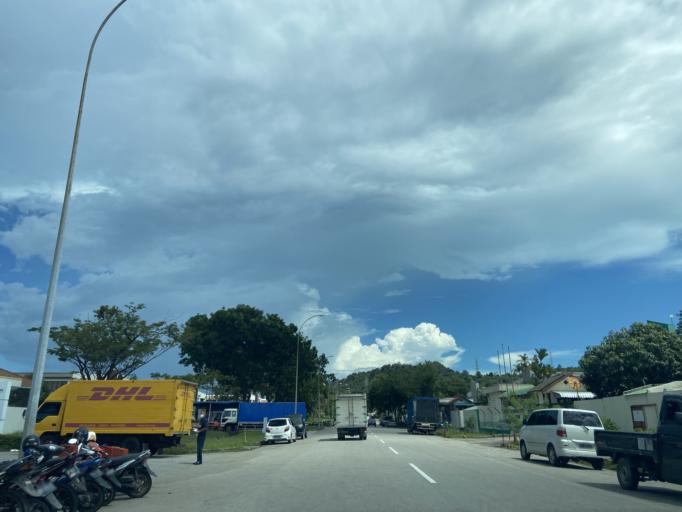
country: SG
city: Singapore
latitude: 1.0579
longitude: 104.0371
